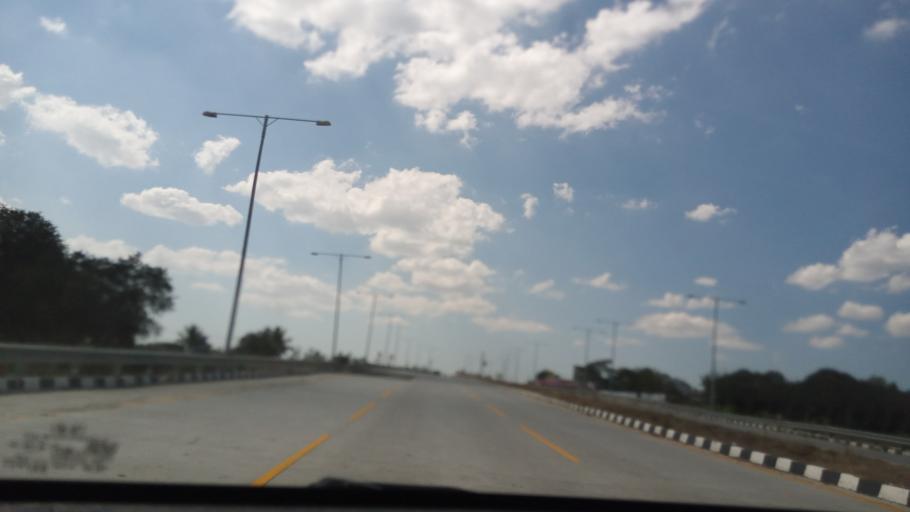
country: IN
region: Andhra Pradesh
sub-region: Chittoor
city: Palmaner
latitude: 13.2140
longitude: 78.7476
